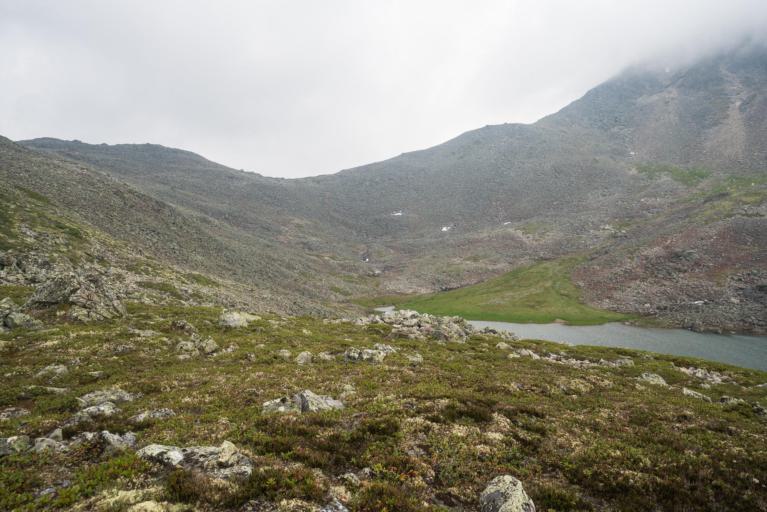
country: RU
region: Transbaikal Territory
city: Kuanda
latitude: 56.7731
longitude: 116.6881
